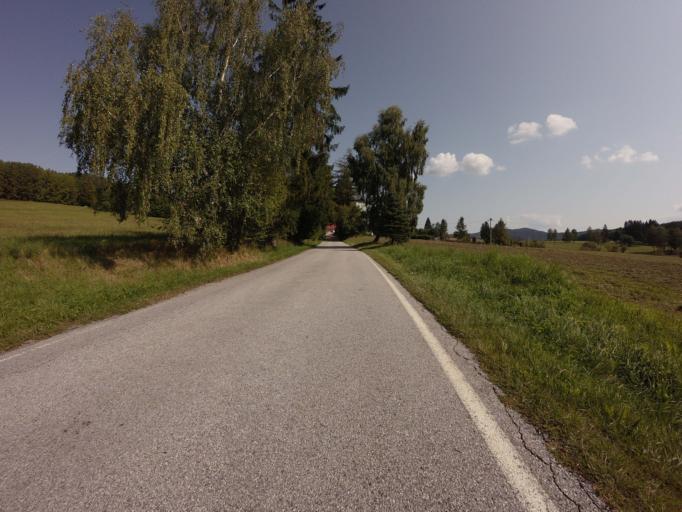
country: CZ
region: Jihocesky
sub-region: Okres Cesky Krumlov
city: Vyssi Brod
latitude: 48.6310
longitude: 14.3401
